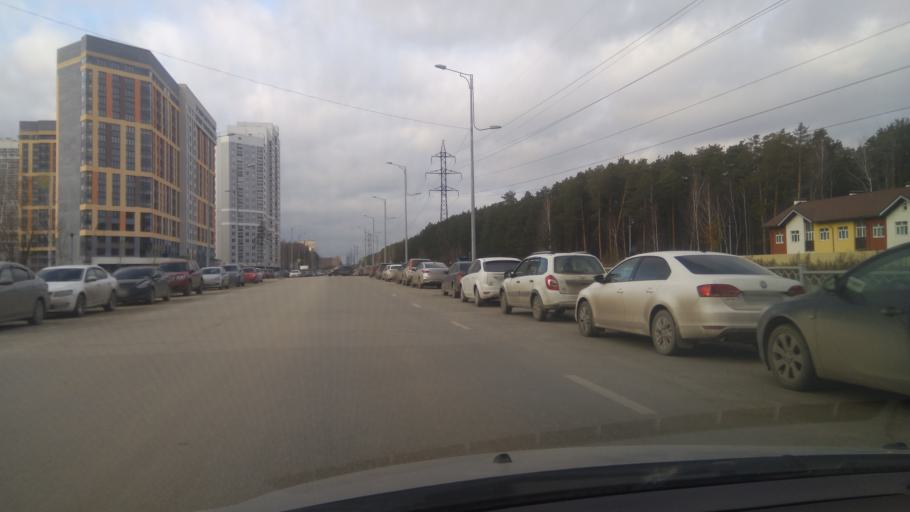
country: RU
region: Sverdlovsk
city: Sovkhoznyy
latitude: 56.7839
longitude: 60.5524
